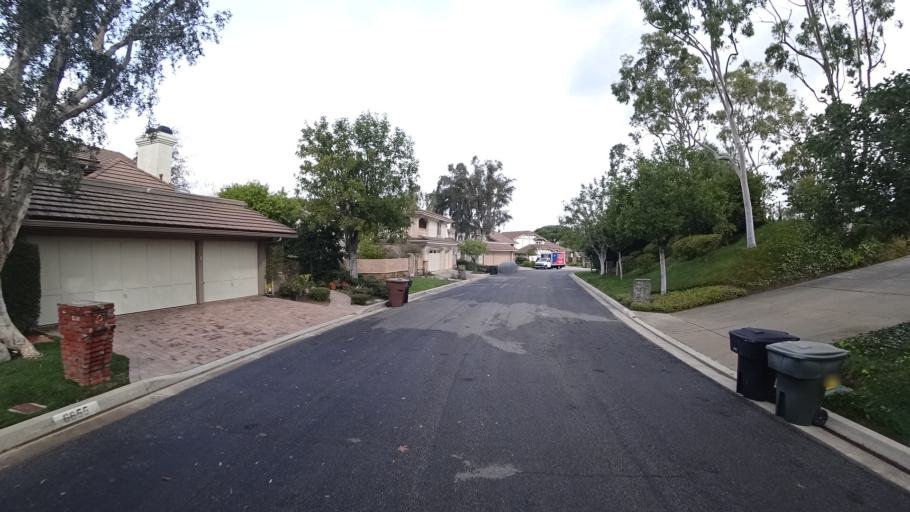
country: US
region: California
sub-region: Orange County
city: Villa Park
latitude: 33.8511
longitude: -117.7675
